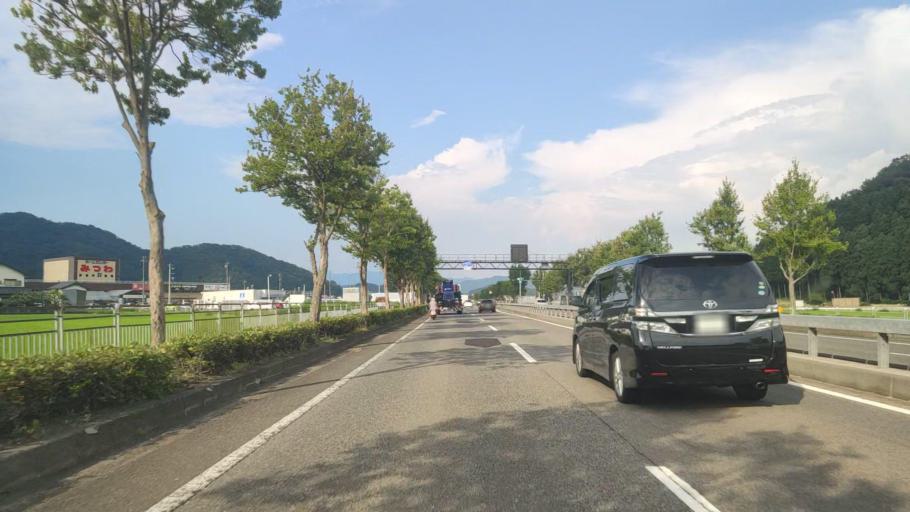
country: JP
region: Fukui
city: Takefu
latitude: 35.8814
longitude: 136.1763
